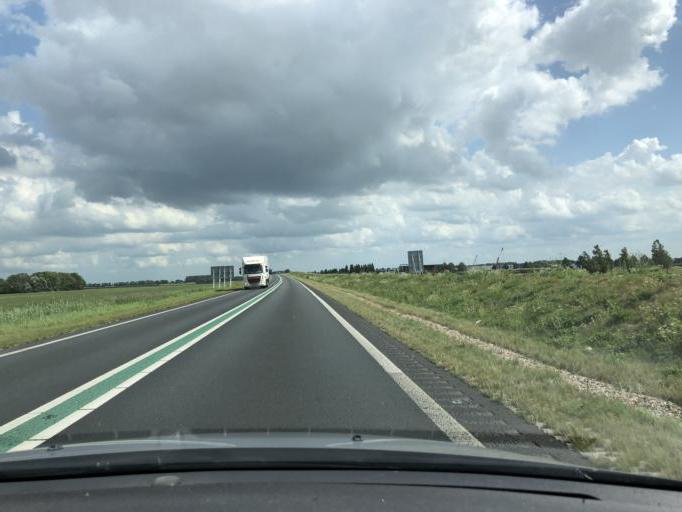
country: NL
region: Flevoland
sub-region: Gemeente Dronten
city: Dronten
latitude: 52.5494
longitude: 5.6995
